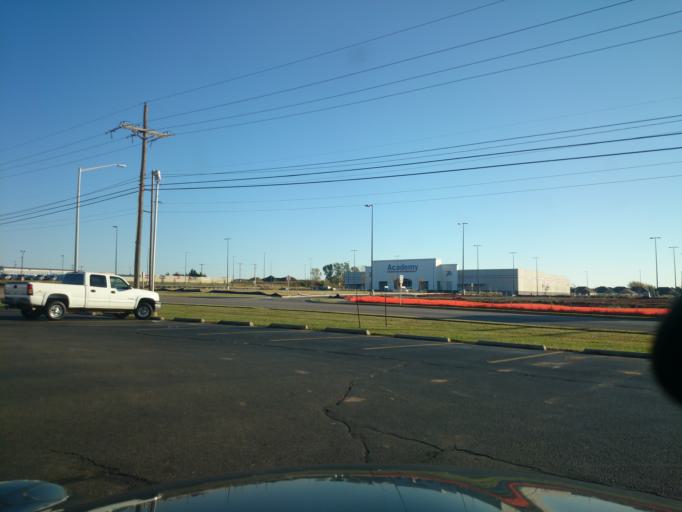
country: US
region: Oklahoma
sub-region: Payne County
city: Stillwater
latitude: 36.1453
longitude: -97.0520
